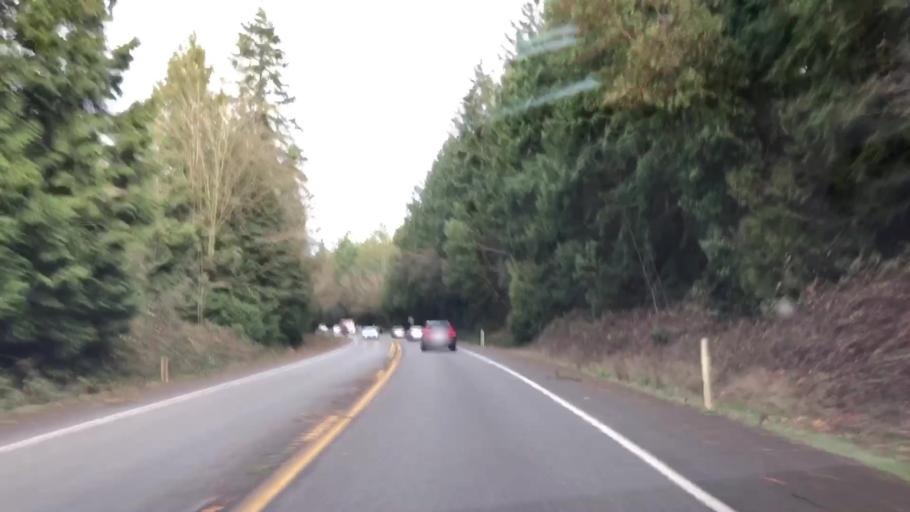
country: US
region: Washington
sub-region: Kitsap County
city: Bainbridge Island
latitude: 47.6589
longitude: -122.5236
